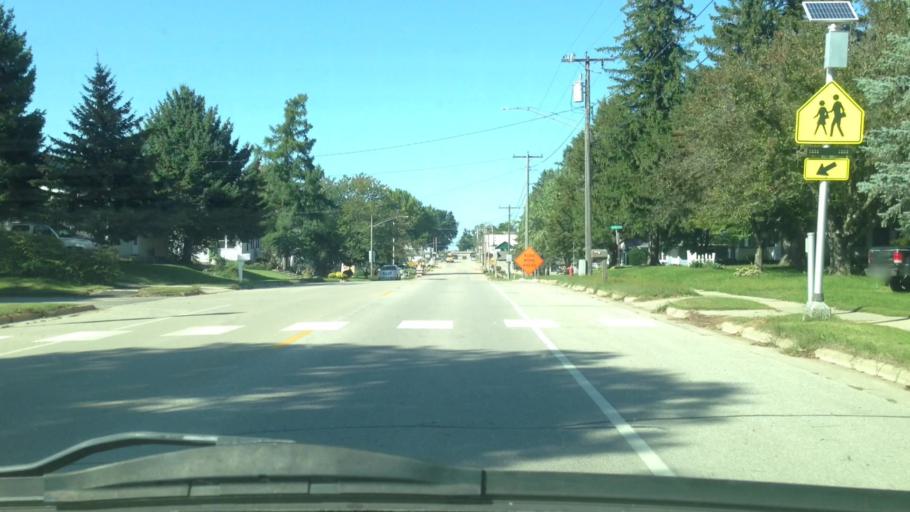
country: US
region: Minnesota
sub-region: Winona County
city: Lewiston
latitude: 43.9812
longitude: -91.8691
